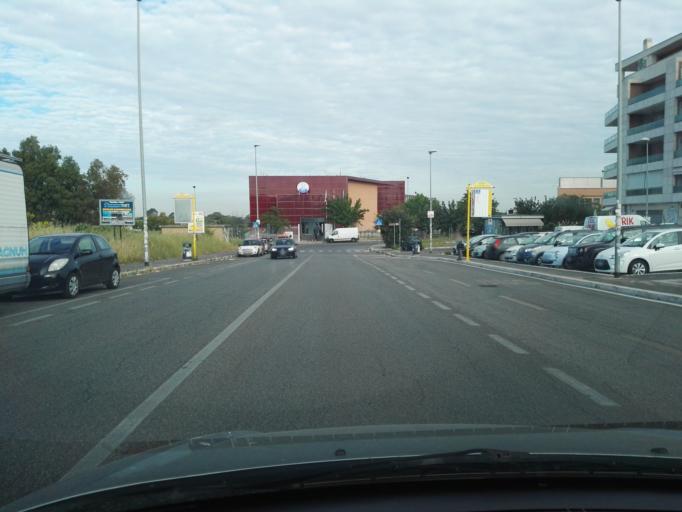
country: IT
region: Latium
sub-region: Citta metropolitana di Roma Capitale
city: Selcetta
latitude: 41.7666
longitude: 12.4710
